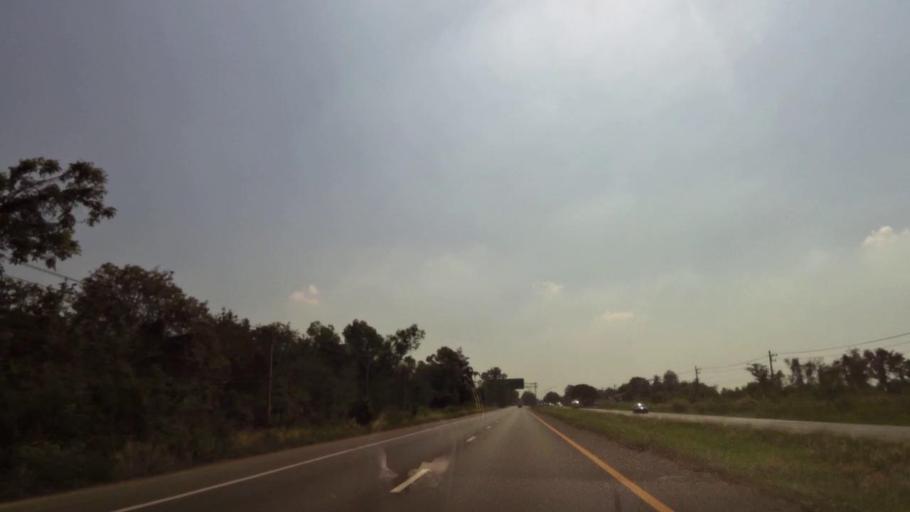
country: TH
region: Phichit
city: Bueng Na Rang
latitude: 16.1971
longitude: 100.1282
